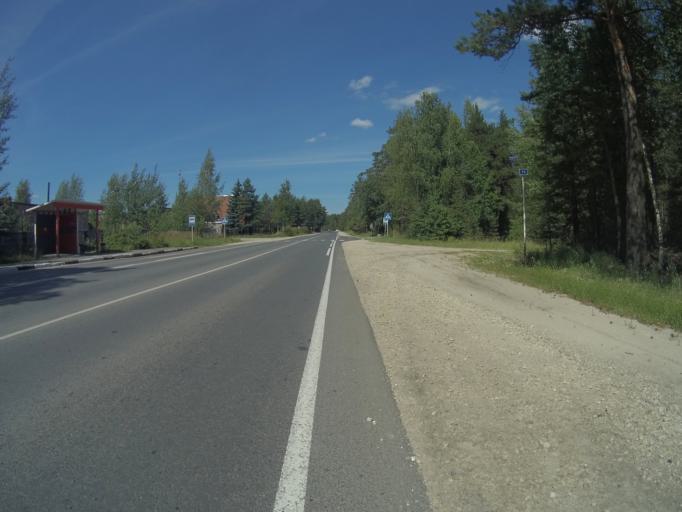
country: RU
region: Vladimir
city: Raduzhnyy
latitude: 56.0252
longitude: 40.3809
